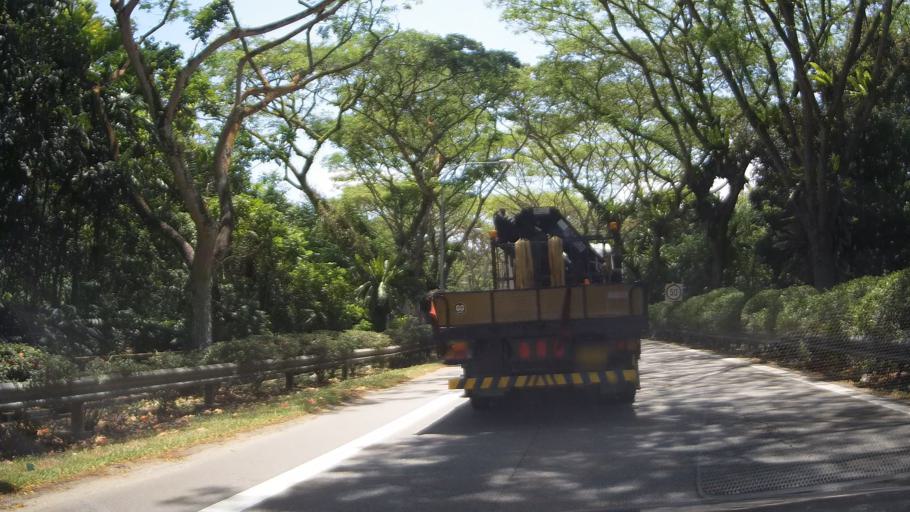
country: MY
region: Johor
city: Johor Bahru
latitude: 1.3661
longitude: 103.7094
